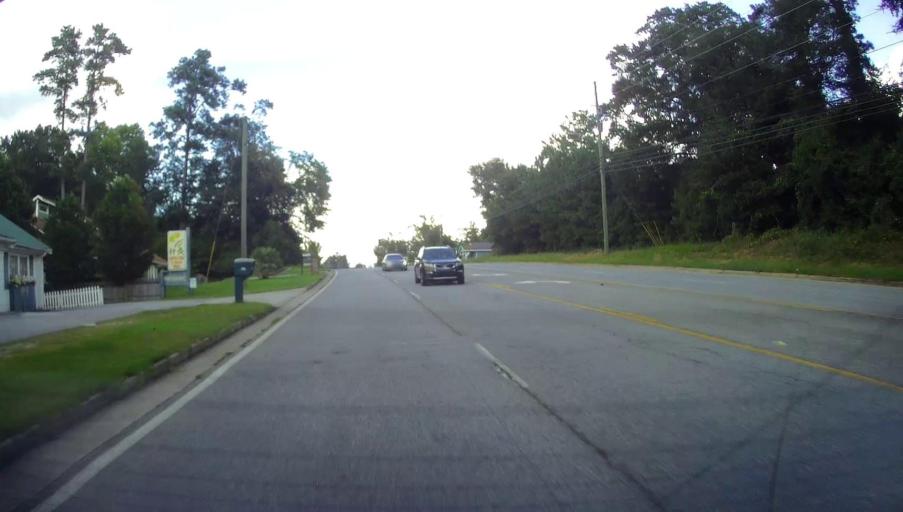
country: US
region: Georgia
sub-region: Muscogee County
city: Columbus
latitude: 32.5314
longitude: -84.9087
